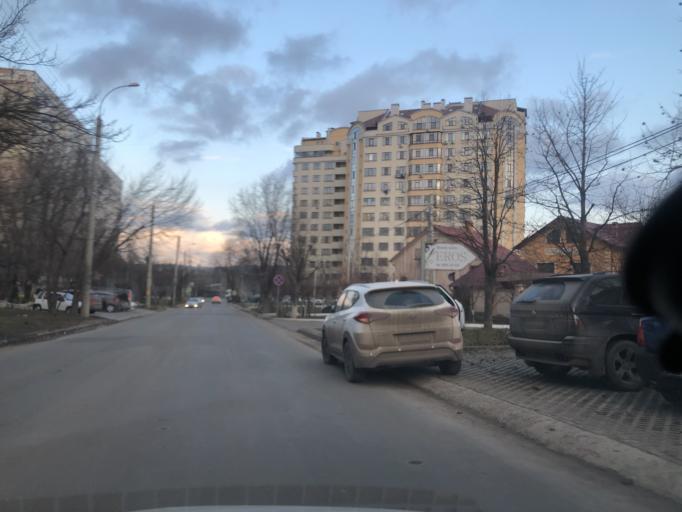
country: MD
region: Chisinau
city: Chisinau
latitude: 47.0385
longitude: 28.8957
